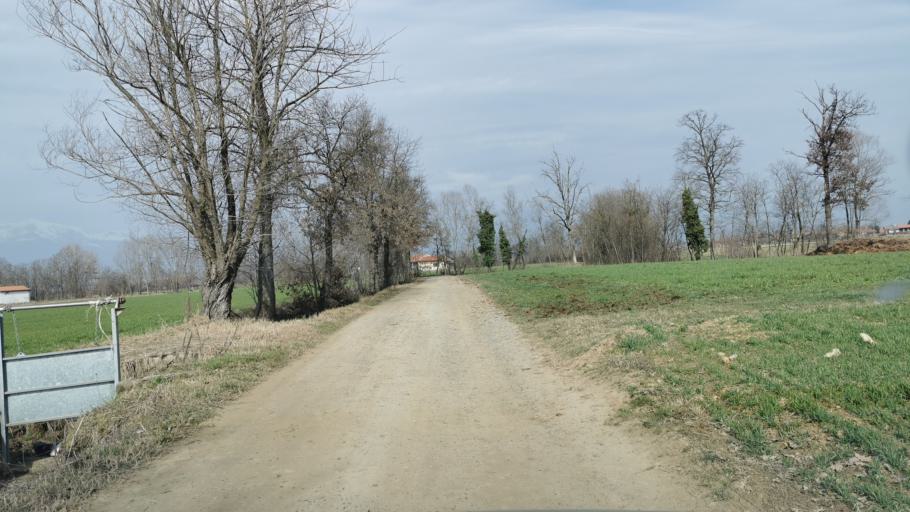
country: IT
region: Piedmont
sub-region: Provincia di Torino
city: Front
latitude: 45.2823
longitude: 7.6974
